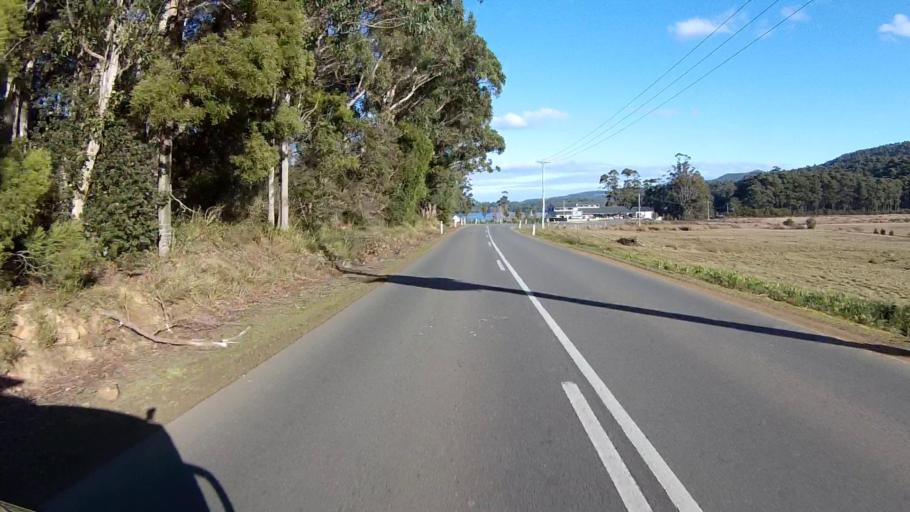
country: AU
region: Tasmania
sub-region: Clarence
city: Sandford
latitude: -43.1045
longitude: 147.8642
